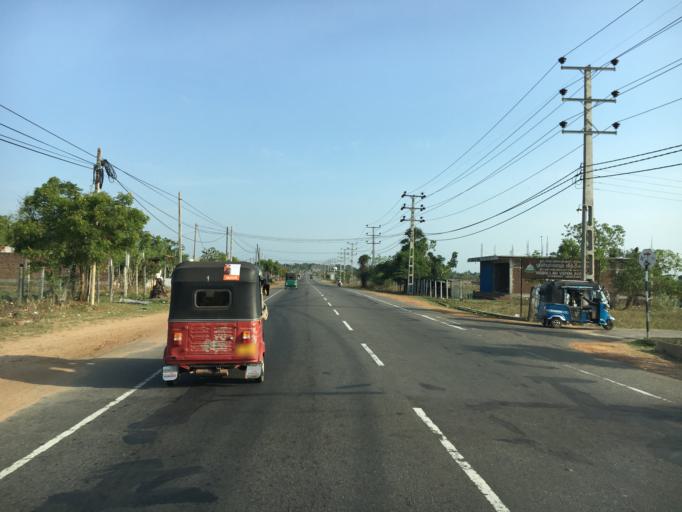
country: LK
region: Eastern Province
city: Eravur Town
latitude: 7.9325
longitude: 81.5113
